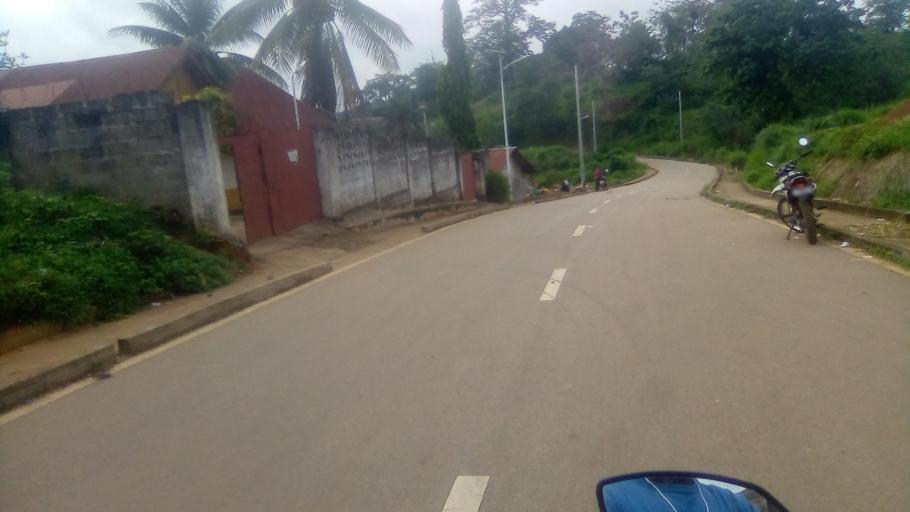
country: SL
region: Eastern Province
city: Kailahun
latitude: 8.2765
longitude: -10.5727
